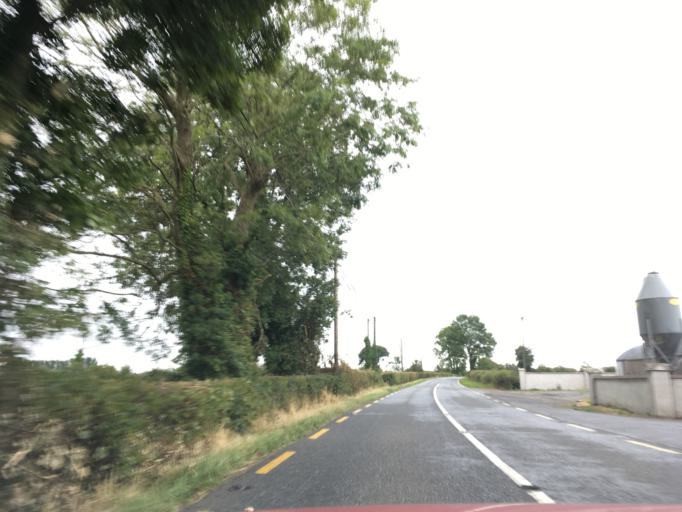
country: IE
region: Munster
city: Fethard
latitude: 52.4271
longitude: -7.7760
